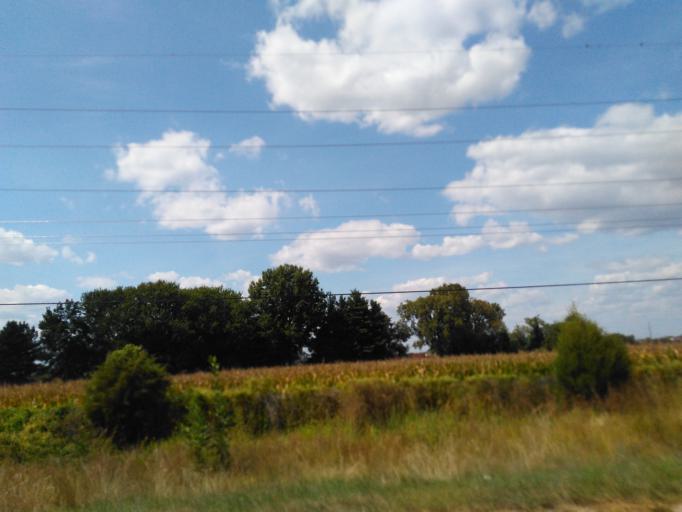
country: US
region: Illinois
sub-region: Saint Clair County
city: Dupo
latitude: 38.4952
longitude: -90.2151
